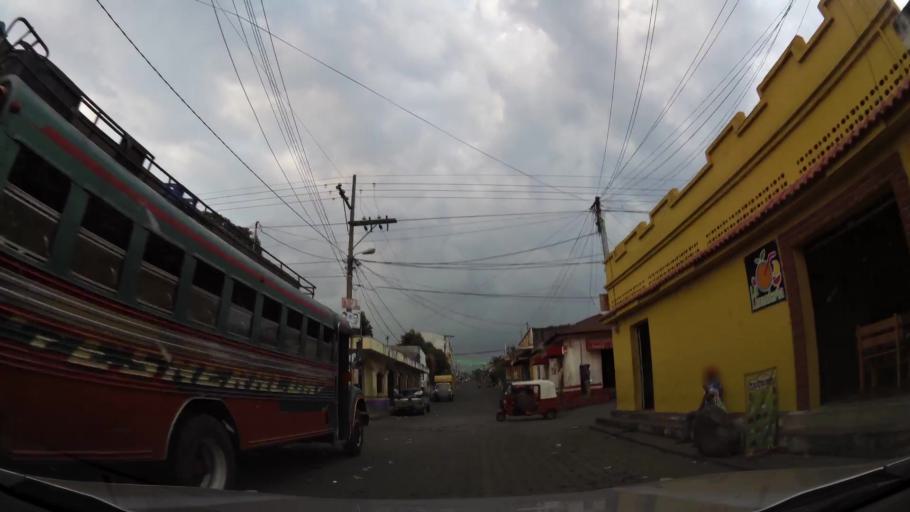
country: GT
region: Escuintla
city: Siquinala
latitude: 14.3070
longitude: -90.9660
